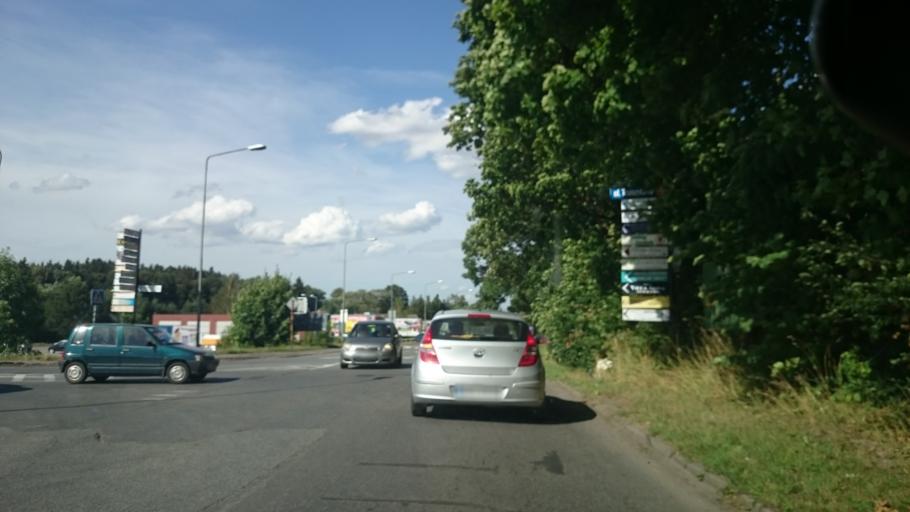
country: PL
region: Lower Silesian Voivodeship
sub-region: Powiat klodzki
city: Polanica-Zdroj
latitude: 50.4088
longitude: 16.5162
